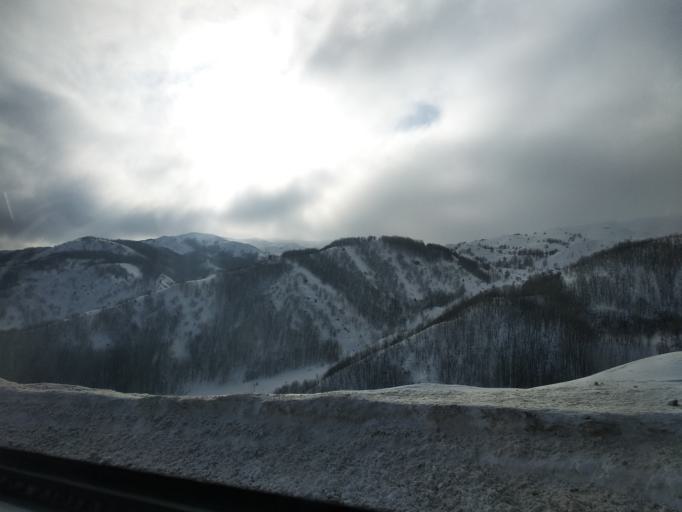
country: TR
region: Erzincan
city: Catalarmut
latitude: 39.8958
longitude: 39.3880
